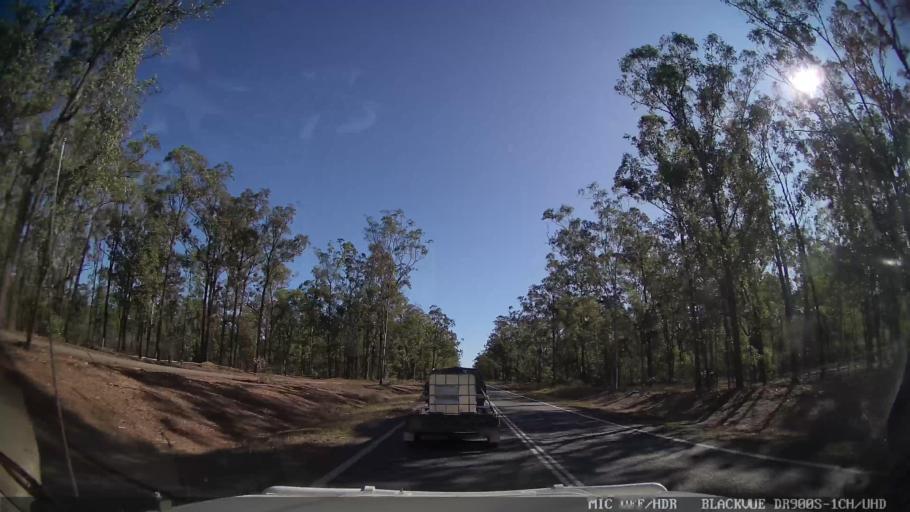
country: AU
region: Queensland
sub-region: Bundaberg
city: Childers
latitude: -25.2161
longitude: 152.0750
